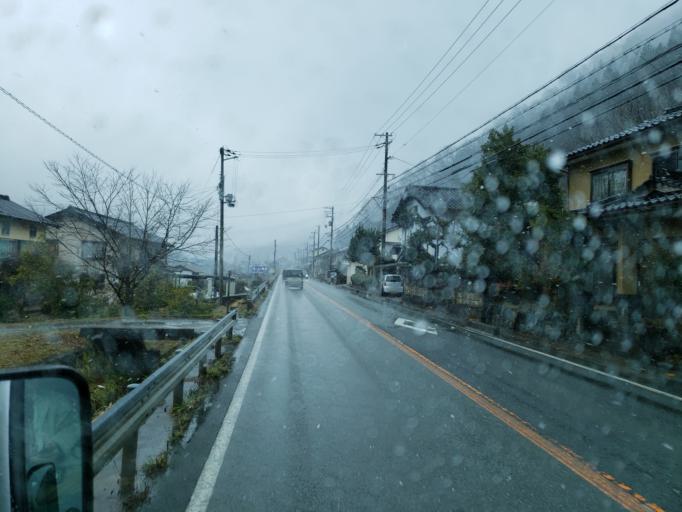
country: JP
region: Hyogo
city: Toyooka
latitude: 35.3869
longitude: 134.6831
